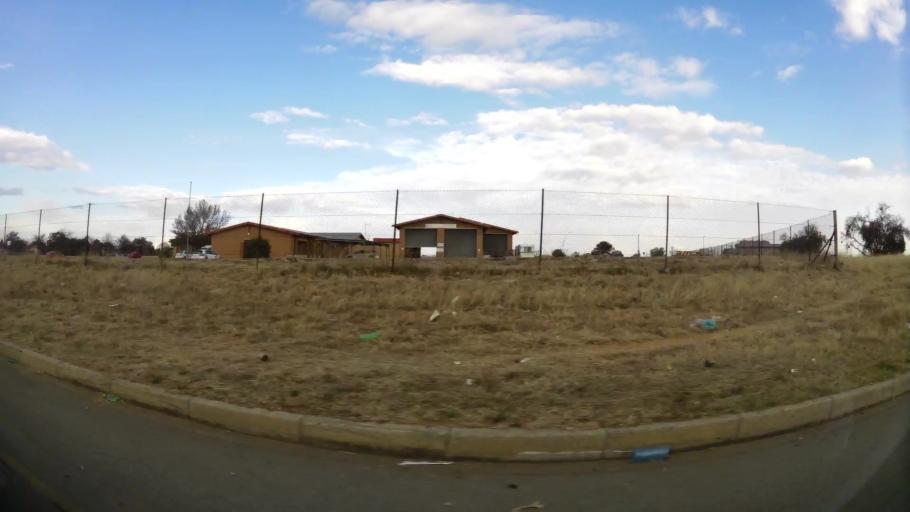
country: ZA
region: Orange Free State
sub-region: Lejweleputswa District Municipality
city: Welkom
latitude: -28.0022
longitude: 26.7370
